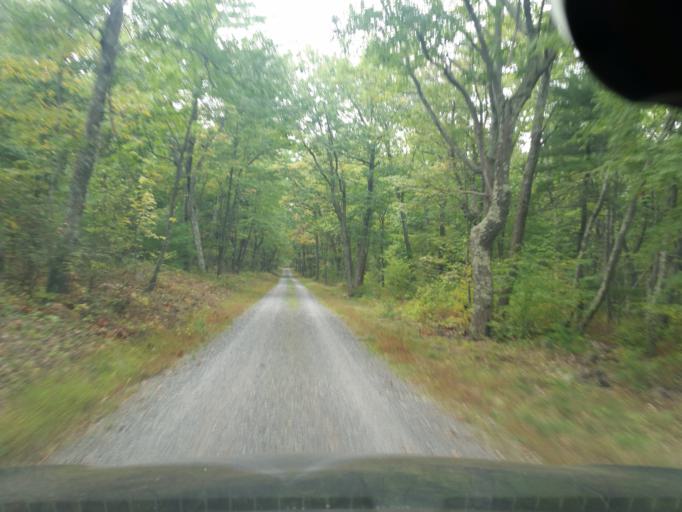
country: US
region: Pennsylvania
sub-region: Lycoming County
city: Jersey Shore
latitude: 41.0845
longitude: -77.1833
